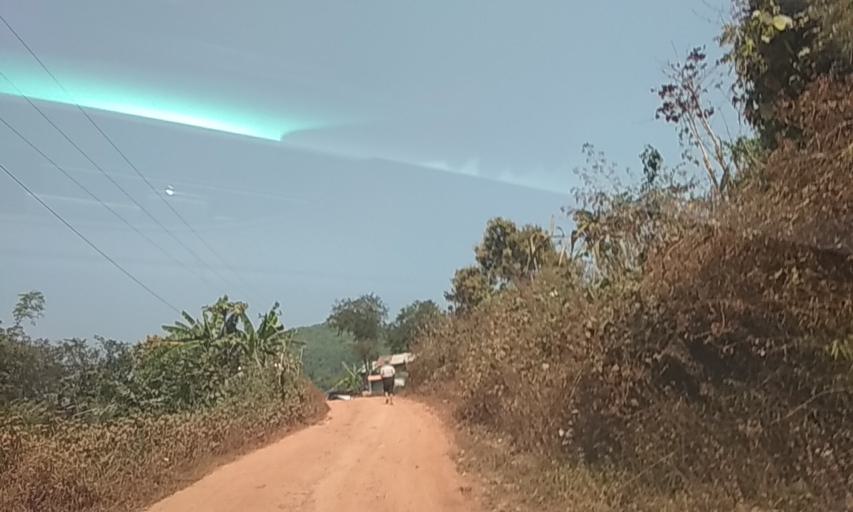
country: CN
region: Yunnan
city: Mengla
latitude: 21.5364
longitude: 101.8308
